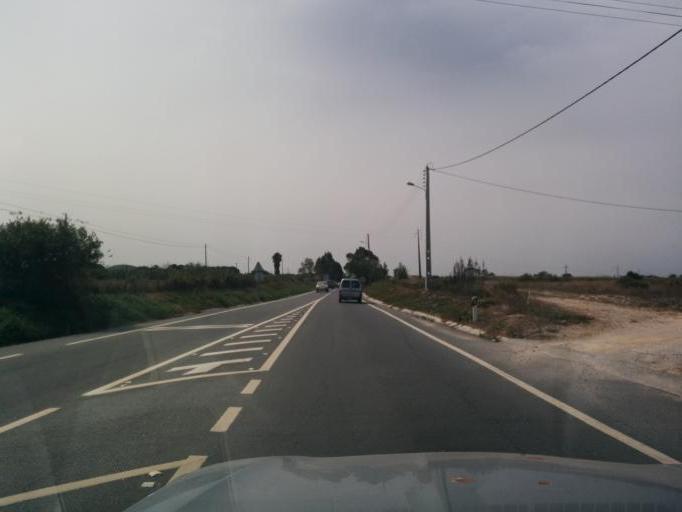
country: PT
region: Beja
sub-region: Odemira
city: Vila Nova de Milfontes
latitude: 37.6543
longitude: -8.7596
